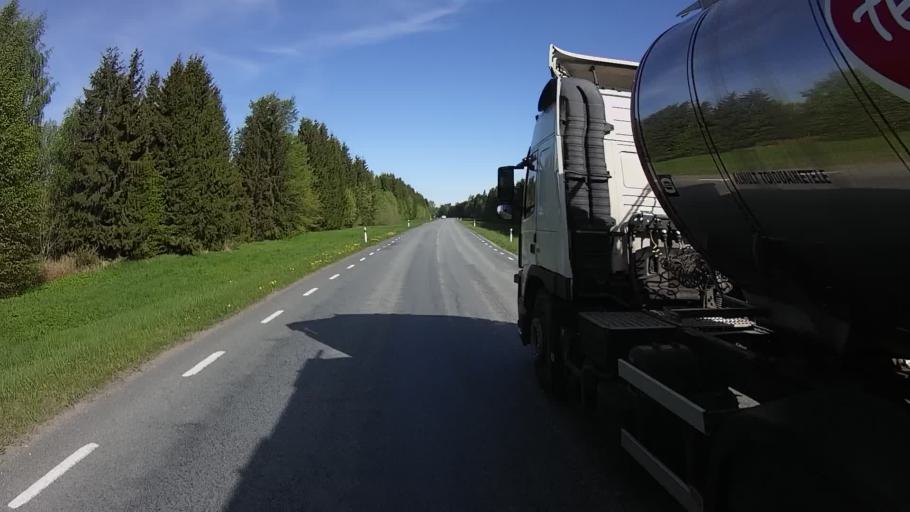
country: EE
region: Polvamaa
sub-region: Polva linn
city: Polva
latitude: 58.2286
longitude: 27.0244
